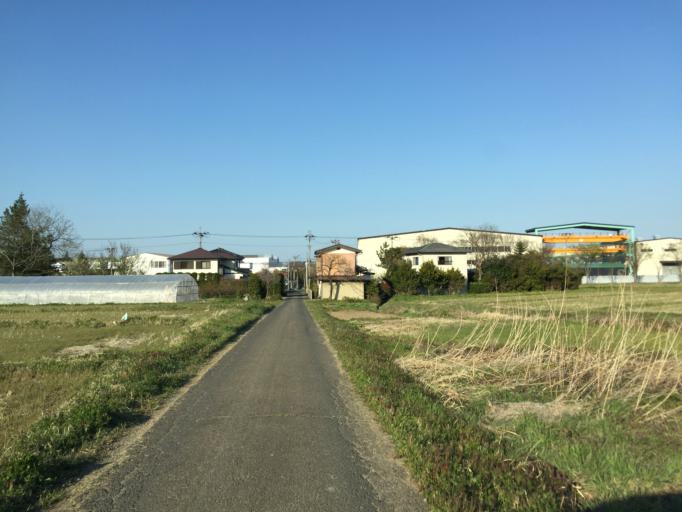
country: JP
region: Fukushima
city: Fukushima-shi
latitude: 37.7366
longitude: 140.3962
